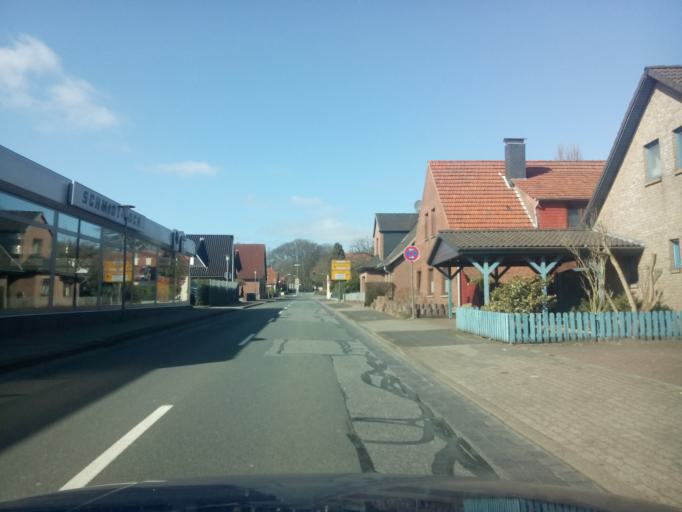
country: DE
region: Lower Saxony
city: Osterholz-Scharmbeck
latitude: 53.2200
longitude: 8.8045
